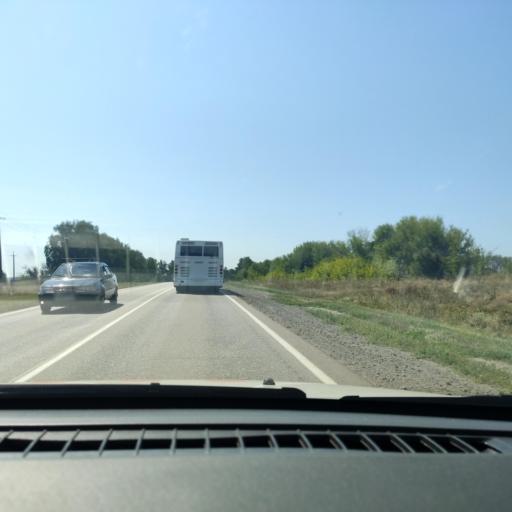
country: RU
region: Voronezj
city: Uryv-Pokrovka
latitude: 51.0696
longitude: 38.9955
